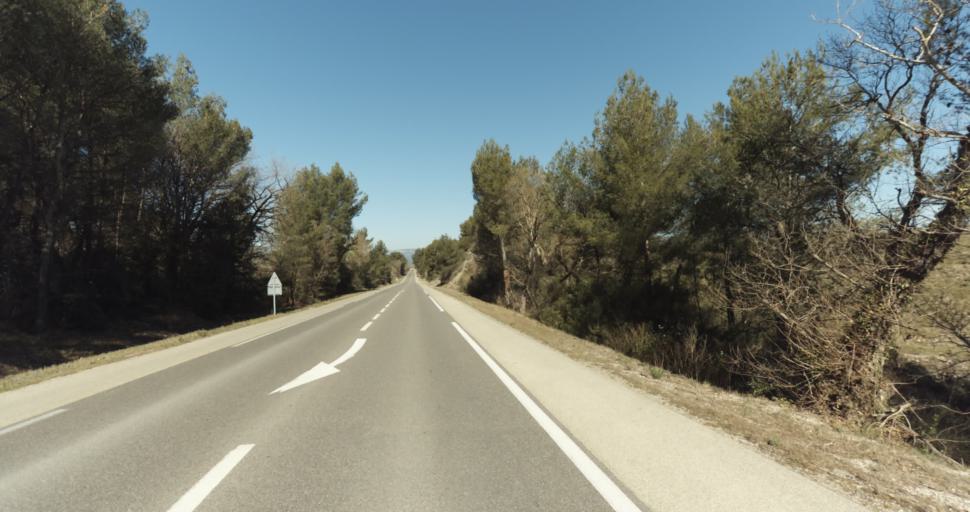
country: FR
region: Provence-Alpes-Cote d'Azur
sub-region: Departement du Vaucluse
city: Cadenet
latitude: 43.7149
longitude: 5.3412
